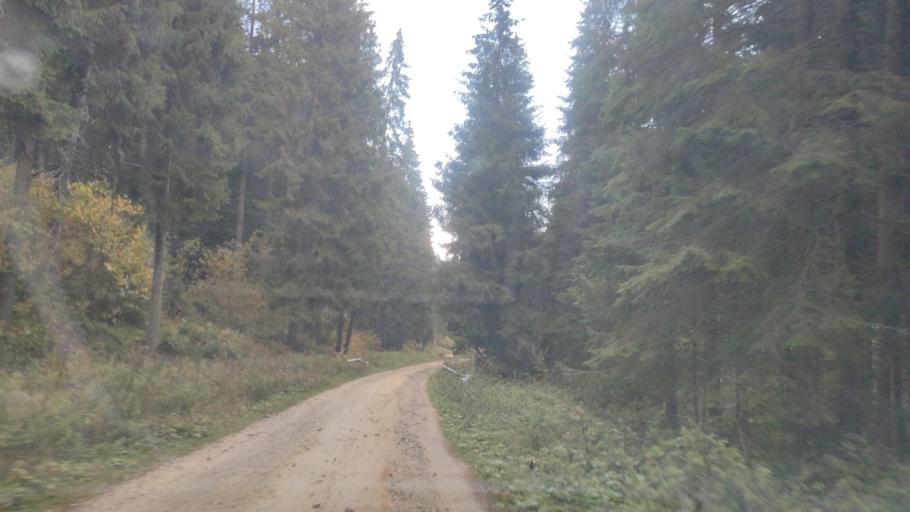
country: RO
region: Harghita
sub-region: Comuna Madaras
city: Madaras
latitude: 46.4760
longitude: 25.6489
